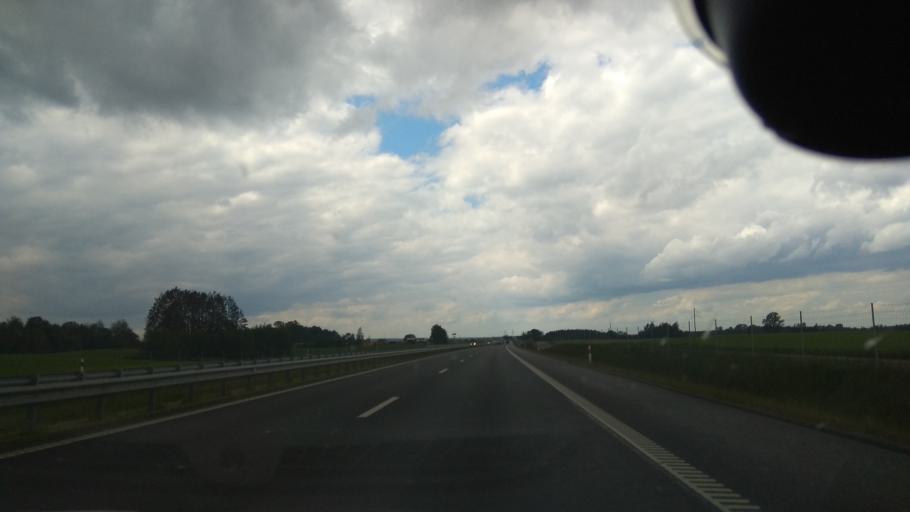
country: LT
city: Kazlu Ruda
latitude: 54.7172
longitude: 23.6571
